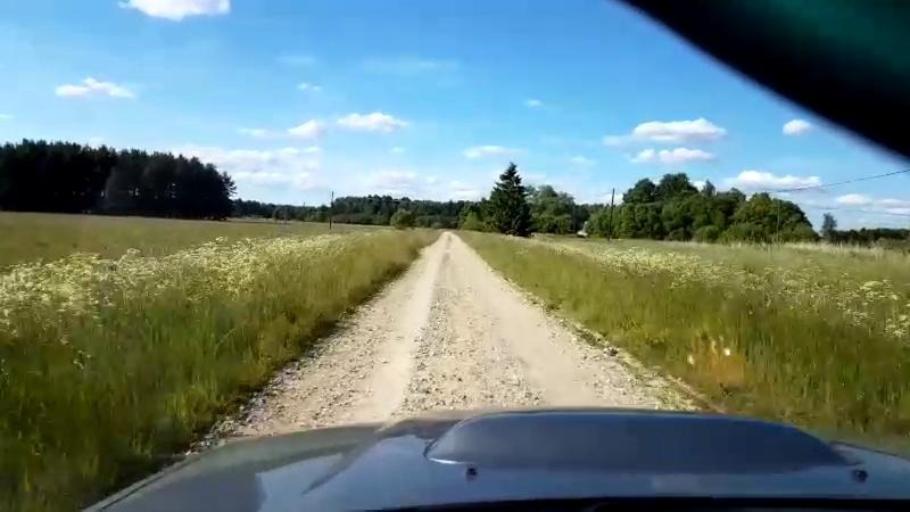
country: EE
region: Paernumaa
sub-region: Sauga vald
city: Sauga
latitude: 58.5086
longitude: 24.5900
